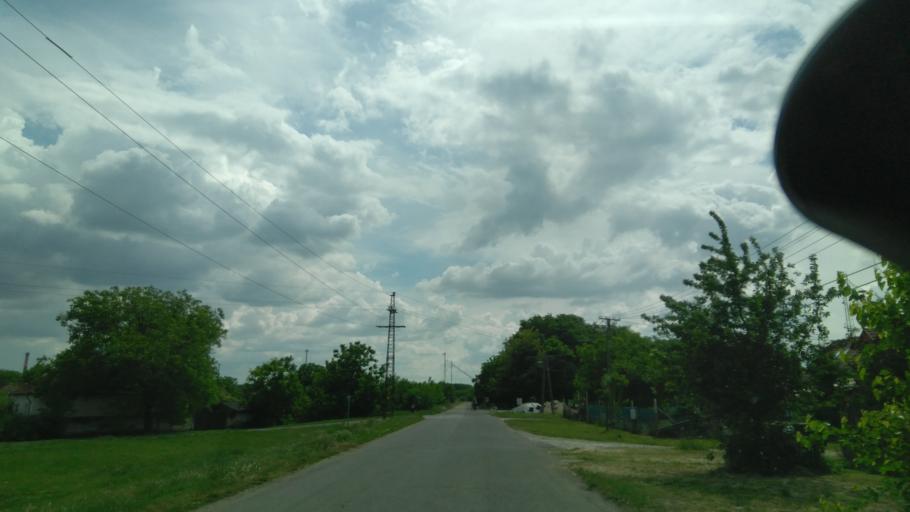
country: HU
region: Bekes
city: Mezohegyes
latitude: 46.3177
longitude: 20.8066
